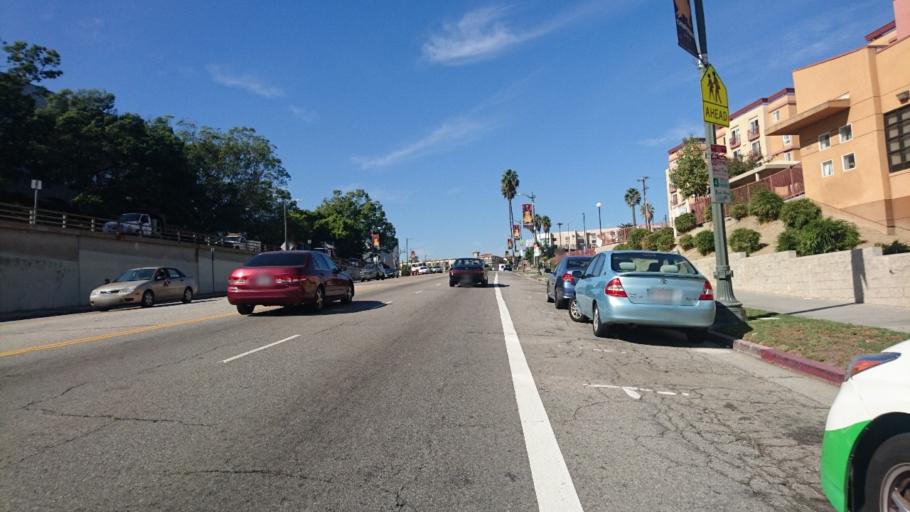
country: US
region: California
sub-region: Los Angeles County
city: Los Angeles
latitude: 34.0595
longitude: -118.2417
